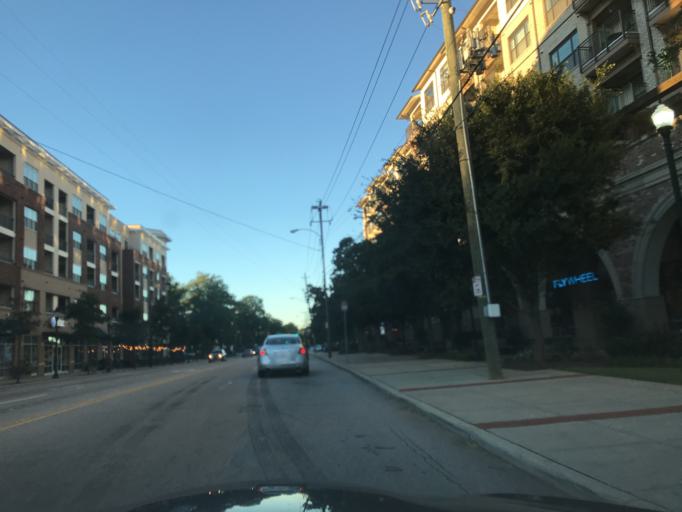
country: US
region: North Carolina
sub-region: Wake County
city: West Raleigh
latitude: 35.7895
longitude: -78.6630
